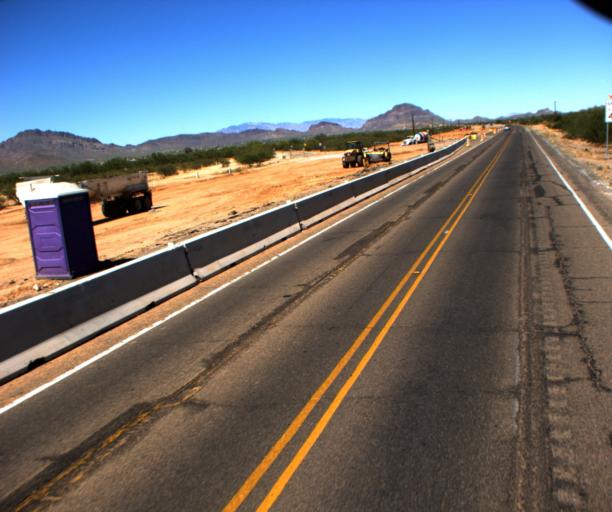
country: US
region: Arizona
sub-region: Pima County
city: Valencia West
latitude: 32.1421
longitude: -111.1458
